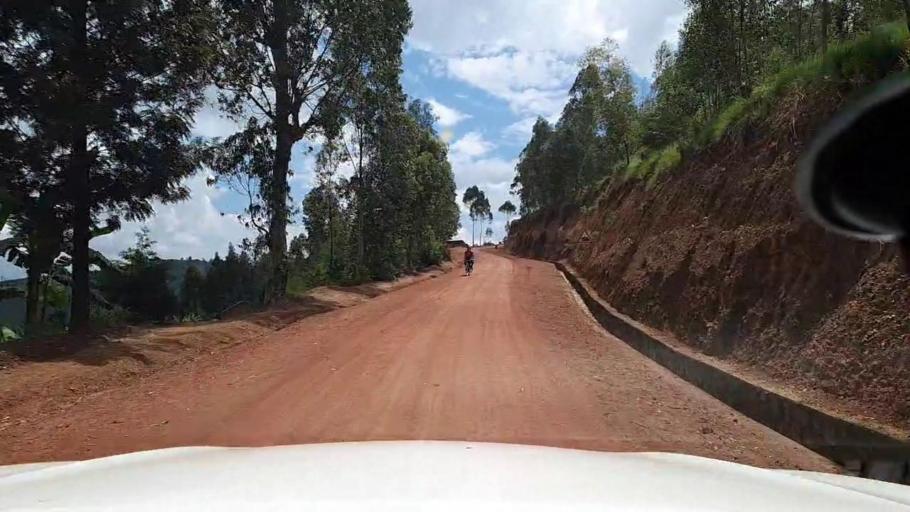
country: RW
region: Northern Province
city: Byumba
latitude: -1.7548
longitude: 29.8506
